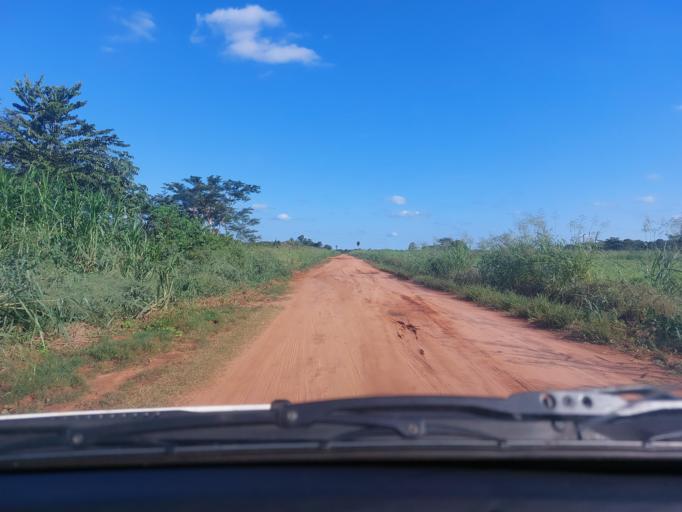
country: PY
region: San Pedro
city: Guayaybi
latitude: -24.5163
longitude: -56.5463
